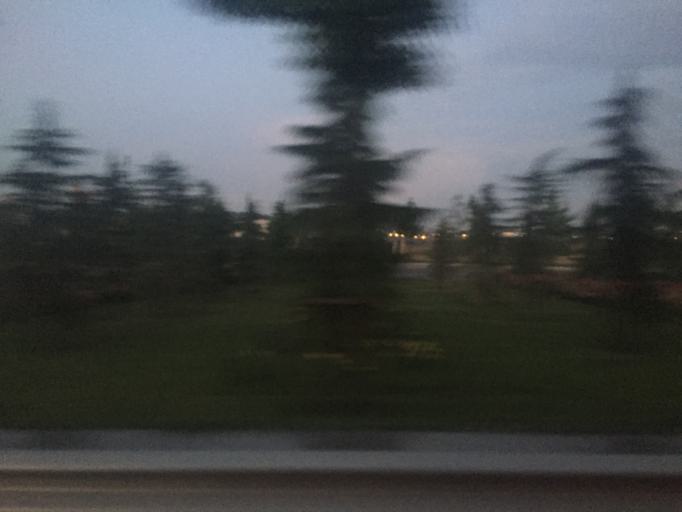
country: TR
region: Istanbul
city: Pendik
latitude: 40.9192
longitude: 29.3121
